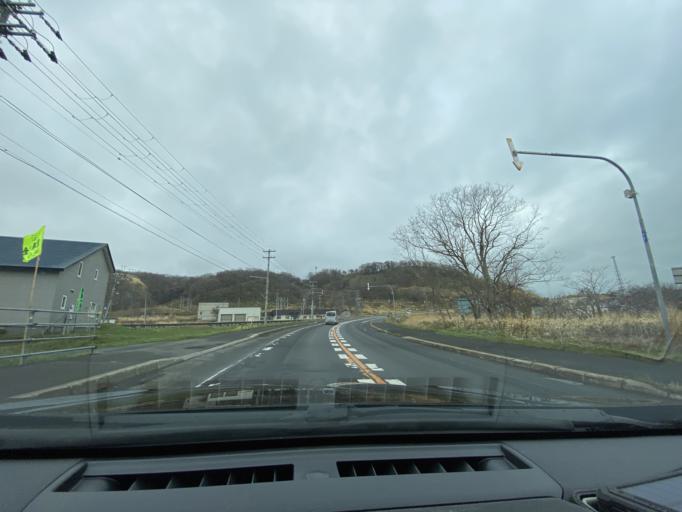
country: JP
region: Hokkaido
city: Ishikari
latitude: 43.3964
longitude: 141.4374
